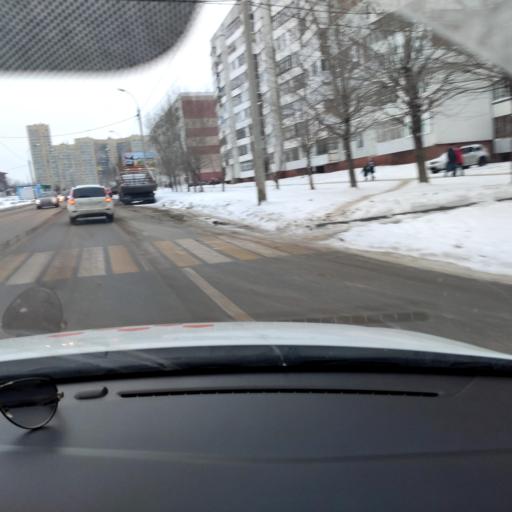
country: RU
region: Tatarstan
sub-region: Gorod Kazan'
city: Kazan
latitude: 55.7755
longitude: 49.2247
